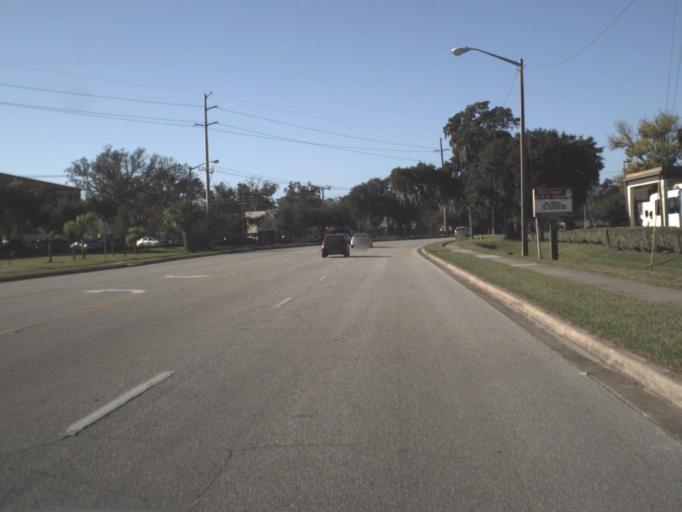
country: US
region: Florida
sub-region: Volusia County
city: Daytona Beach
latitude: 29.2169
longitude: -81.0314
